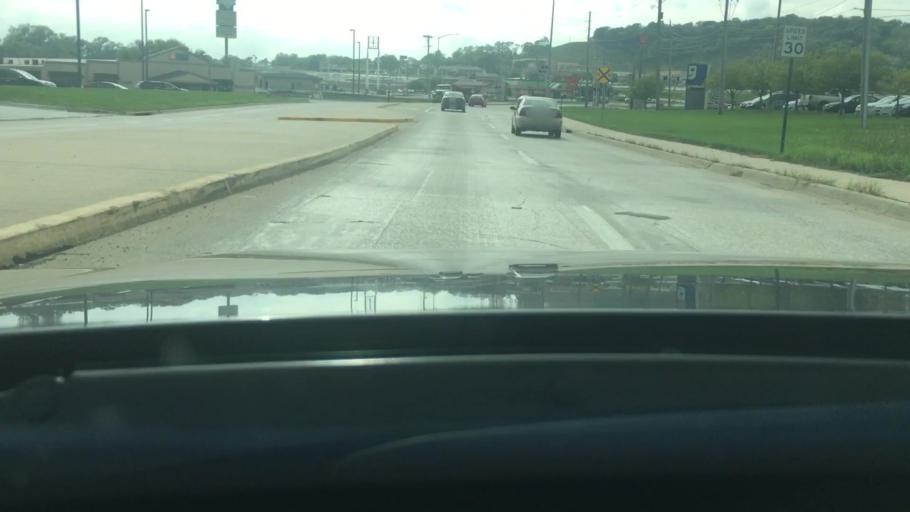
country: US
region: Iowa
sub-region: Pottawattamie County
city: Council Bluffs
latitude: 41.2420
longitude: -95.8191
